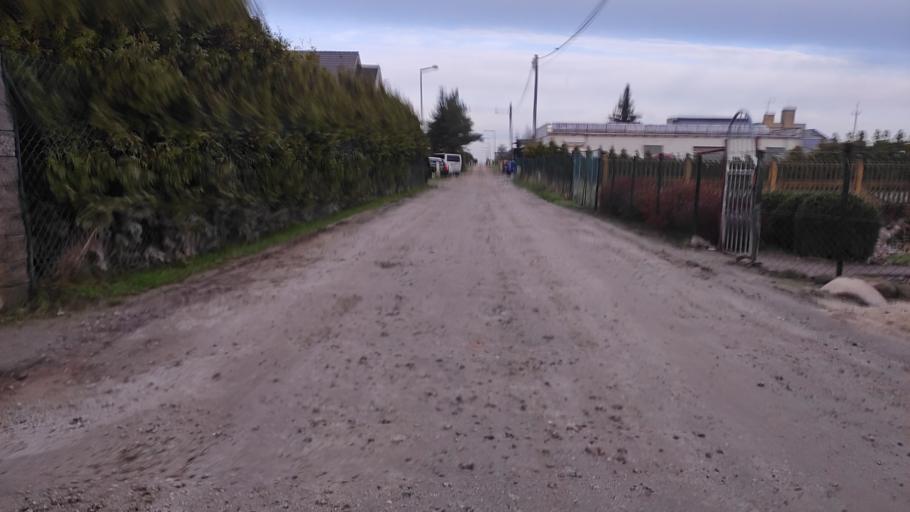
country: PL
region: Greater Poland Voivodeship
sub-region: Powiat poznanski
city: Kleszczewo
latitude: 52.4007
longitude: 17.1572
